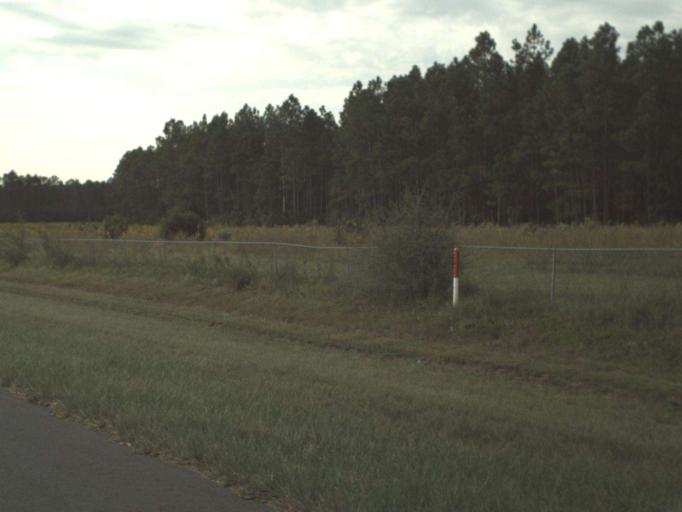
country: US
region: Florida
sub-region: Gulf County
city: Wewahitchka
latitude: 30.1356
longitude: -85.3690
